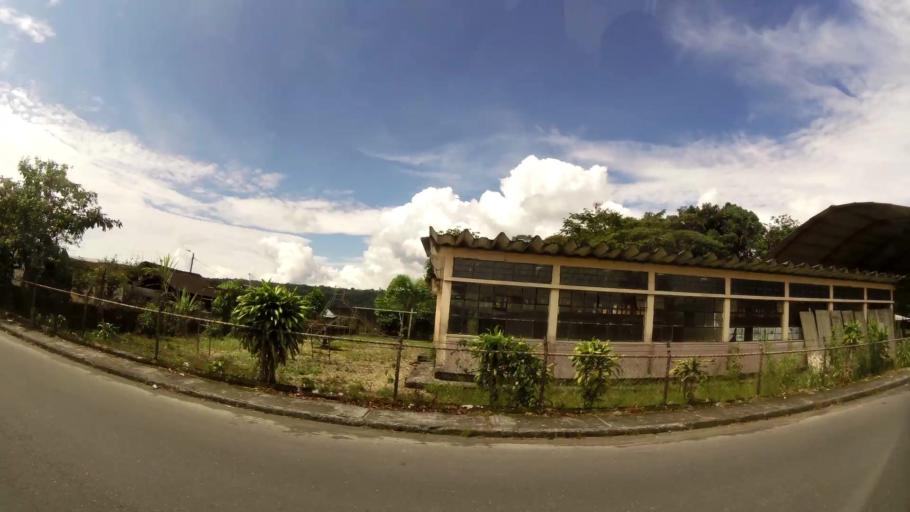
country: EC
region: Pastaza
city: Puyo
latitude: -1.4623
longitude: -78.1110
